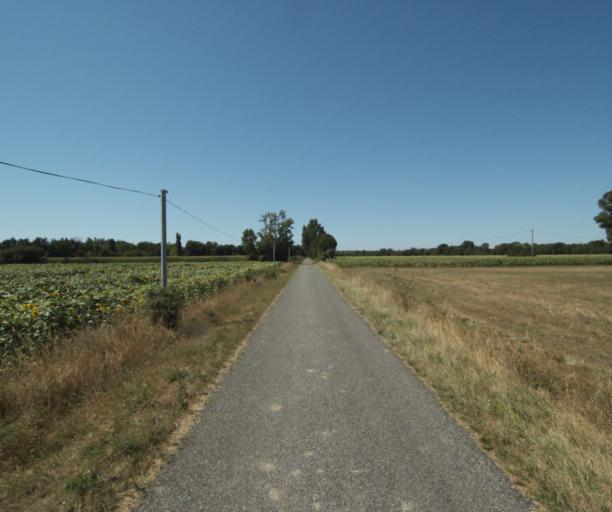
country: FR
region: Midi-Pyrenees
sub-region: Departement de la Haute-Garonne
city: Revel
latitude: 43.4911
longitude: 1.9600
